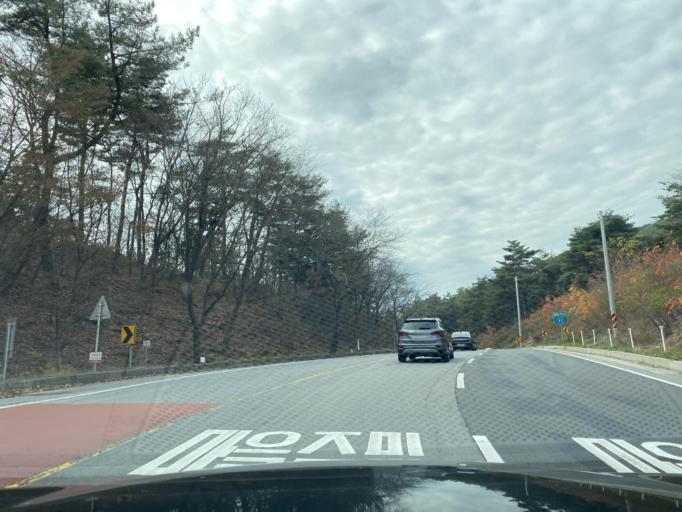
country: KR
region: Chungcheongnam-do
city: Hongsung
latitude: 36.6650
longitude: 126.6353
